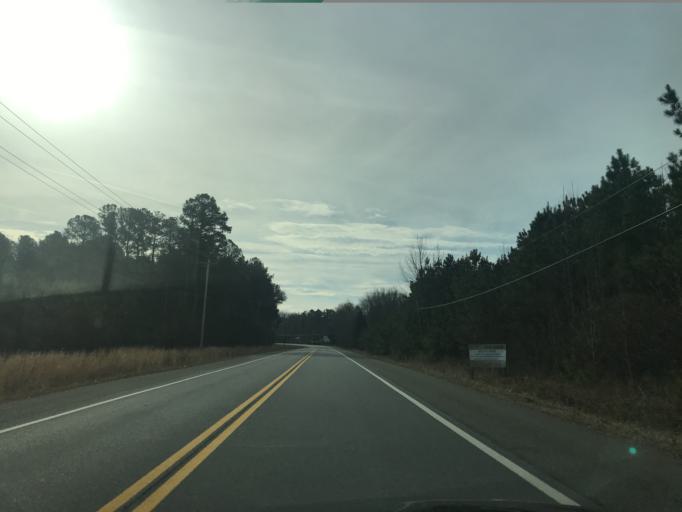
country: US
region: Maryland
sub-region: Charles County
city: Cobb Island
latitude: 38.3191
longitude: -76.8924
